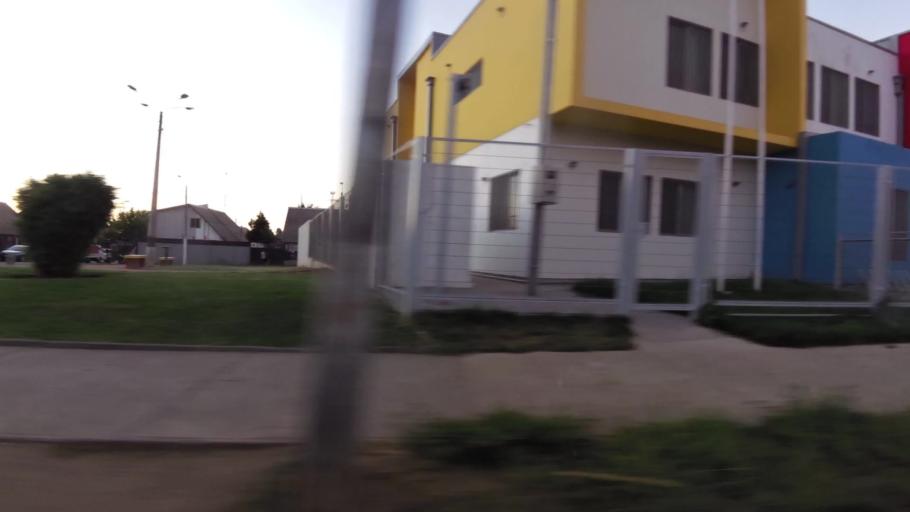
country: CL
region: Maule
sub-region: Provincia de Talca
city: Talca
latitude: -35.4490
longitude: -71.6250
